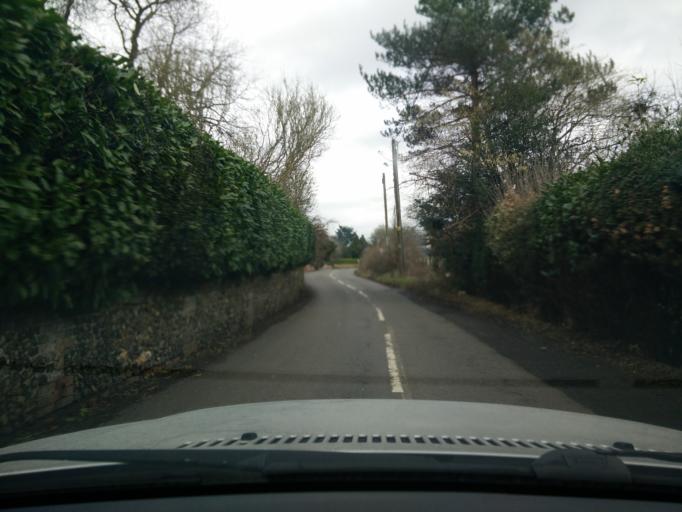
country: GB
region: England
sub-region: Buckinghamshire
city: Amersham
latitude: 51.6527
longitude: -0.6262
